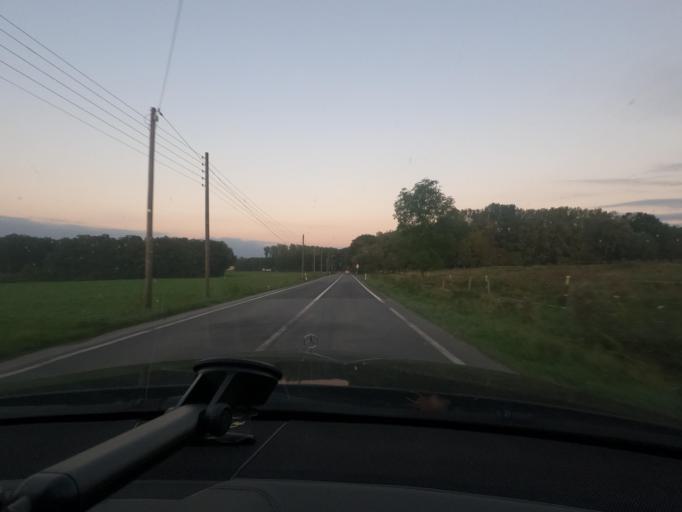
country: DE
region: North Rhine-Westphalia
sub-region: Regierungsbezirk Arnsberg
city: Frondenberg
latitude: 51.4593
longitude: 7.6976
